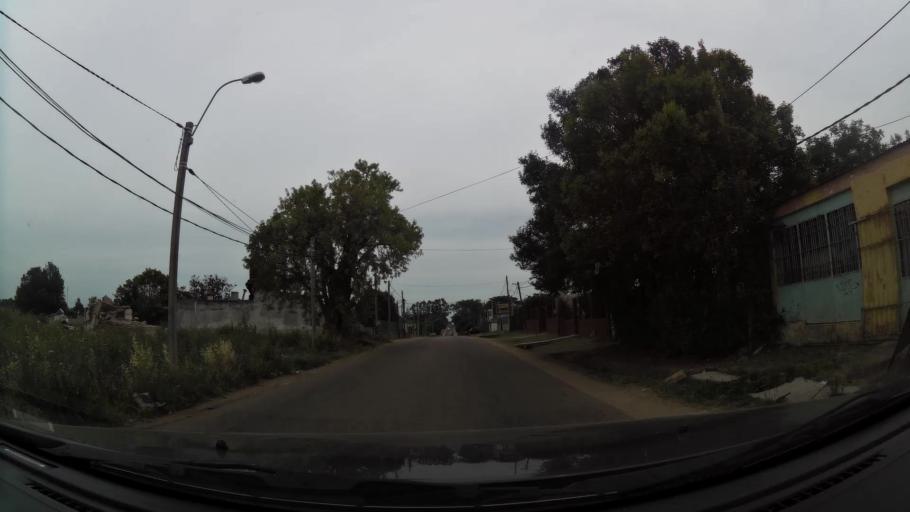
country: UY
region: Canelones
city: Las Piedras
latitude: -34.7350
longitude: -56.2276
